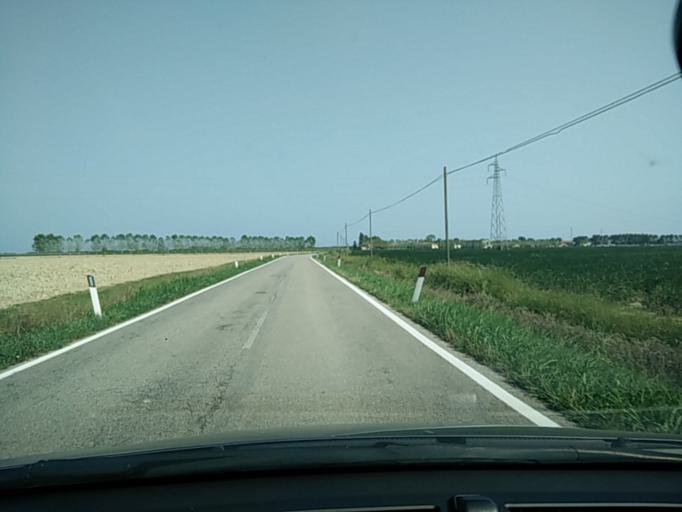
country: IT
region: Veneto
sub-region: Provincia di Venezia
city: Caorle
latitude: 45.6200
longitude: 12.8520
